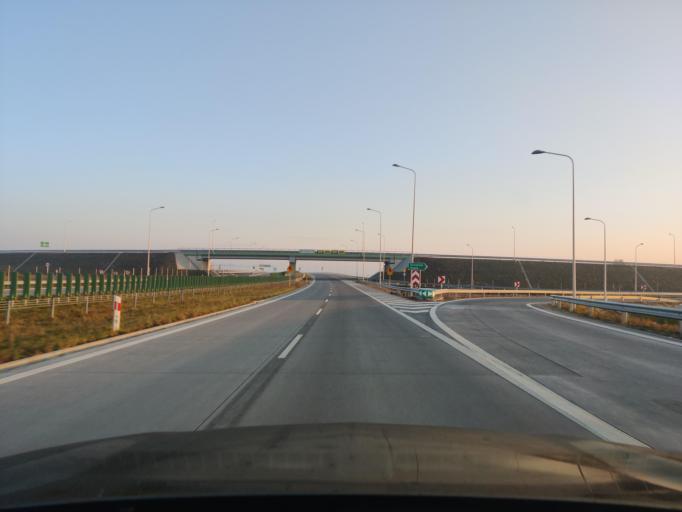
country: PL
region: Masovian Voivodeship
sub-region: Powiat mlawski
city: Wisniewo
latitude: 52.9884
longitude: 20.3450
